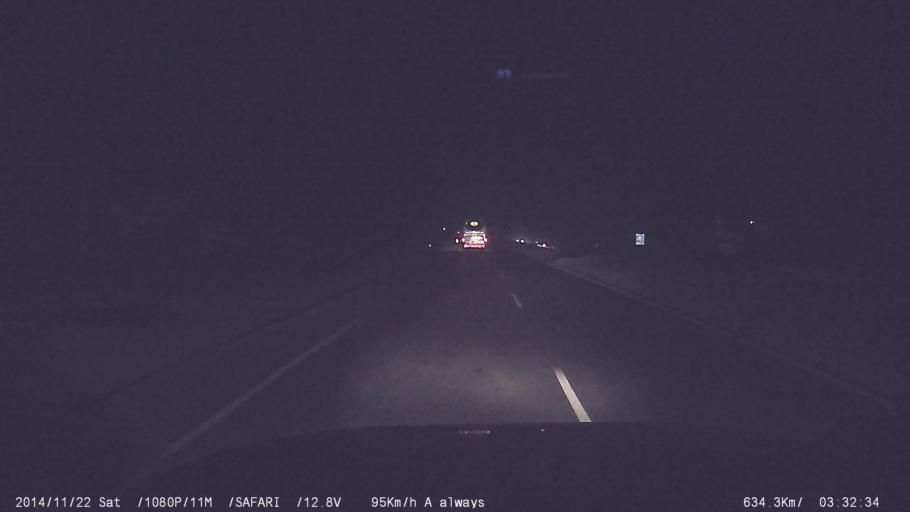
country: IN
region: Tamil Nadu
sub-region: Salem
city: Konganapuram
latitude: 11.5019
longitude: 77.9112
